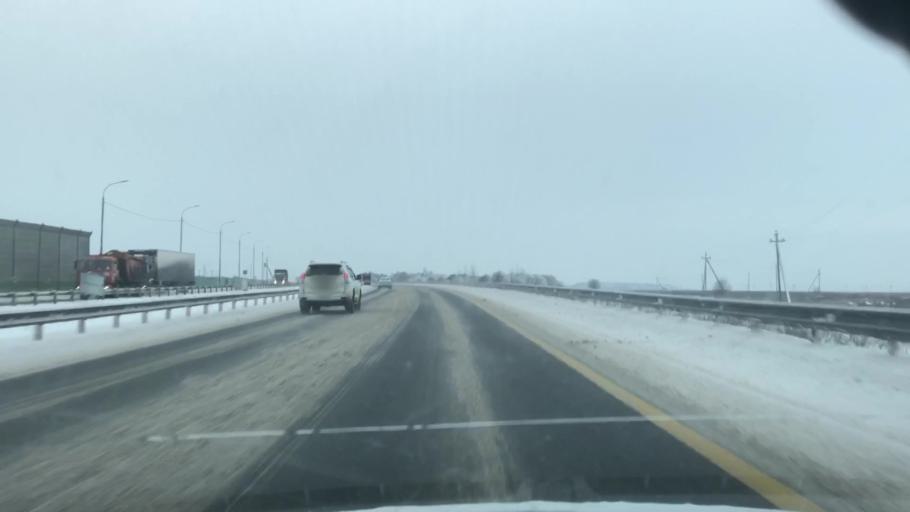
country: RU
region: Moskovskaya
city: Mikhnevo
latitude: 55.1174
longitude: 37.9274
